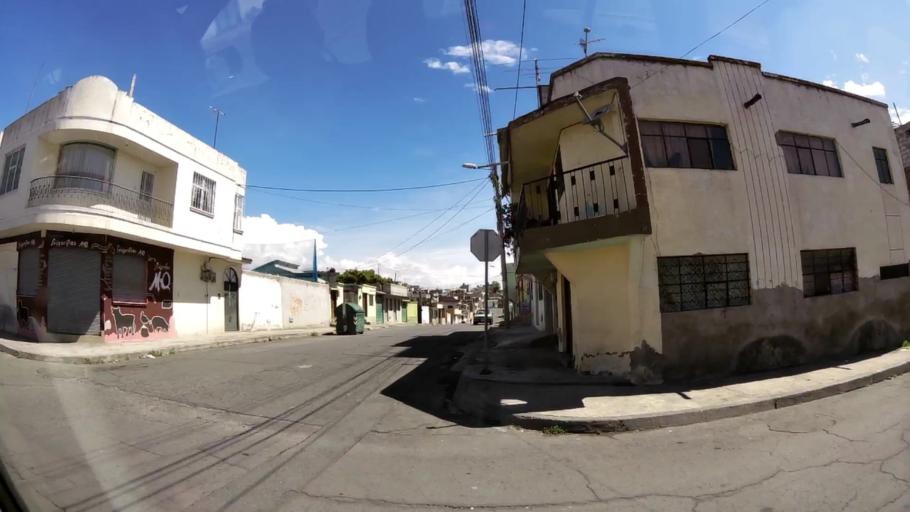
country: EC
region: Chimborazo
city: Riobamba
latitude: -1.6676
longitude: -78.6416
